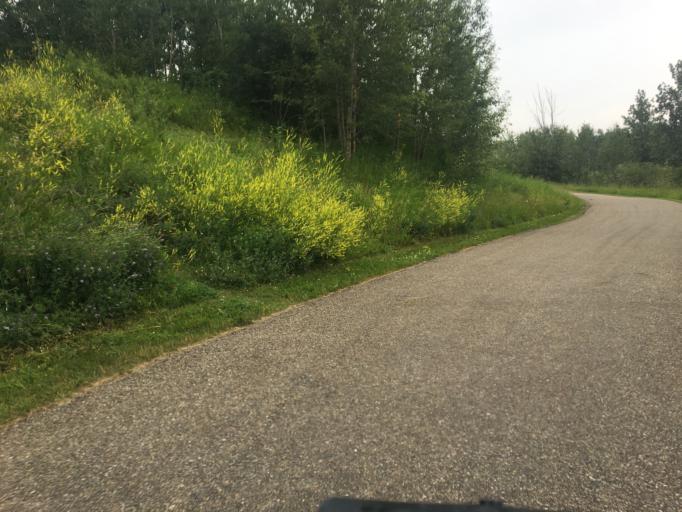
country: CA
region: Alberta
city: Grande Prairie
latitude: 55.1608
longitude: -118.8029
